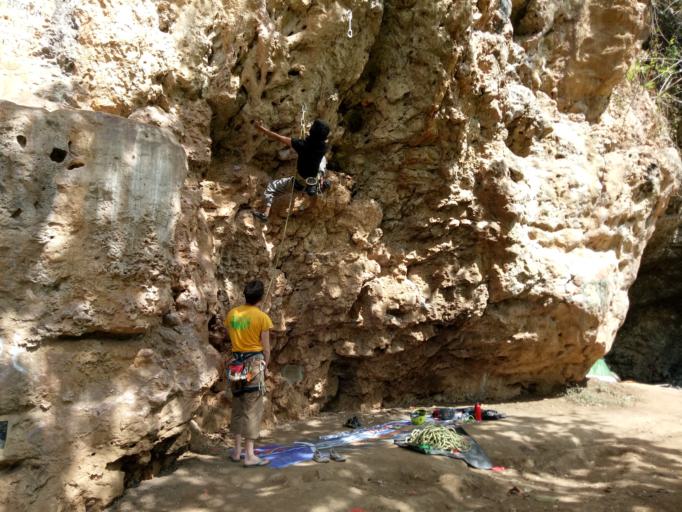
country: ID
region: East Java
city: Sumuran
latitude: -8.2008
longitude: 112.5315
